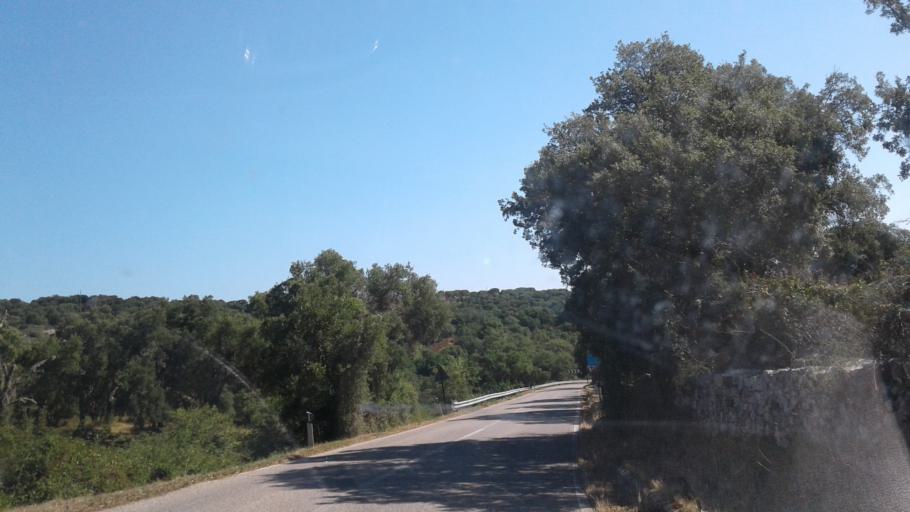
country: IT
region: Sardinia
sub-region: Provincia di Olbia-Tempio
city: Aggius
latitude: 40.9458
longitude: 9.0879
